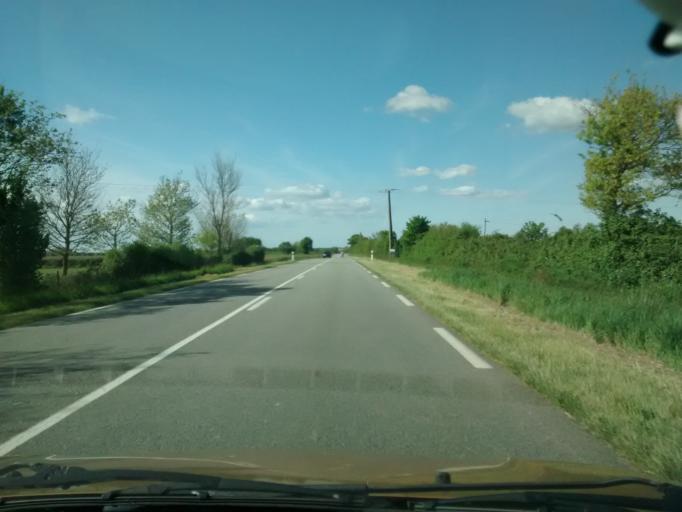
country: FR
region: Pays de la Loire
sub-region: Departement de la Vendee
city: Rocheserviere
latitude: 46.9542
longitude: -1.5135
